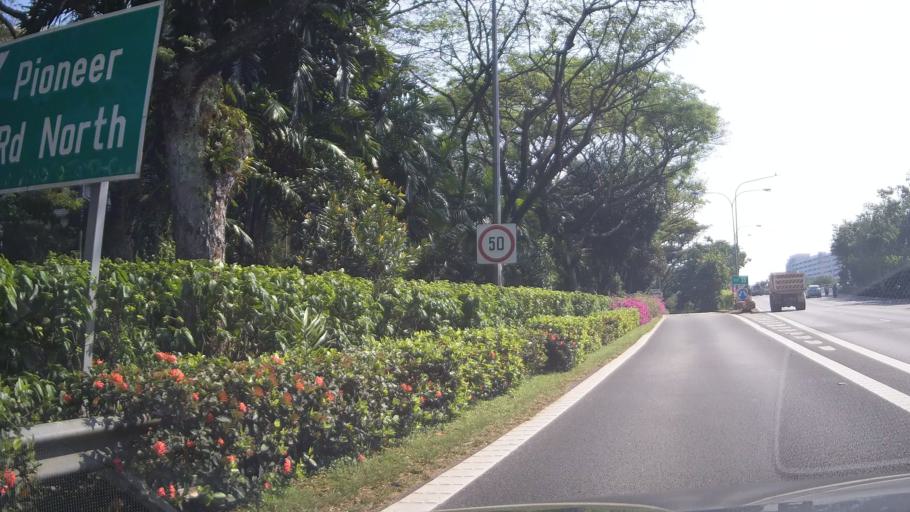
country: MY
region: Johor
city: Johor Bahru
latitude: 1.3450
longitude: 103.6888
